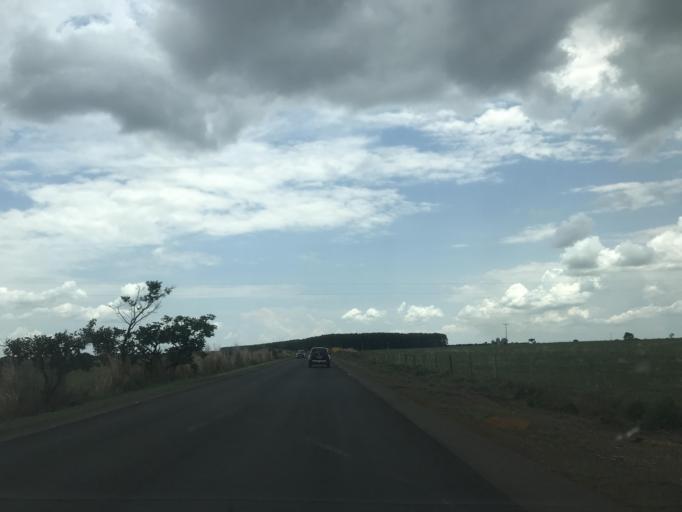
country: BR
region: Goias
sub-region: Vianopolis
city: Vianopolis
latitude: -16.9193
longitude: -48.5560
